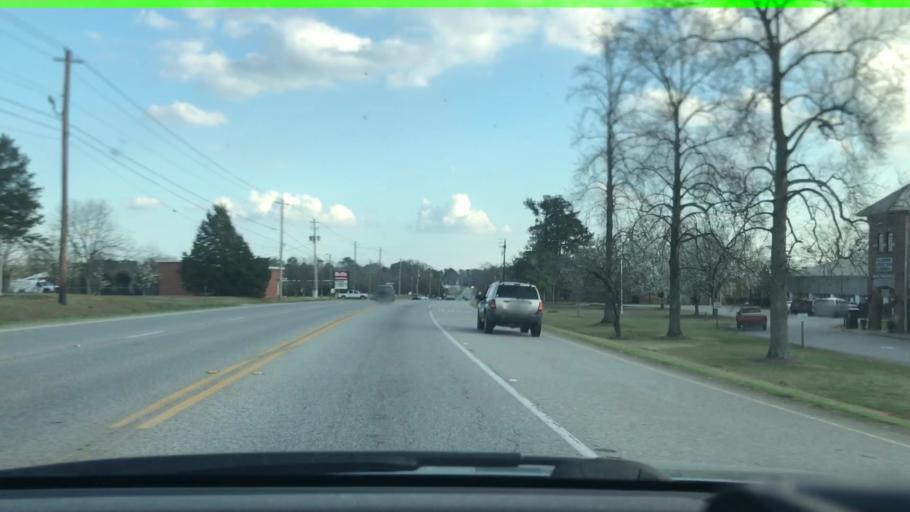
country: US
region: Georgia
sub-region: Oglethorpe County
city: Lexington
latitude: 33.8850
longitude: -83.1249
